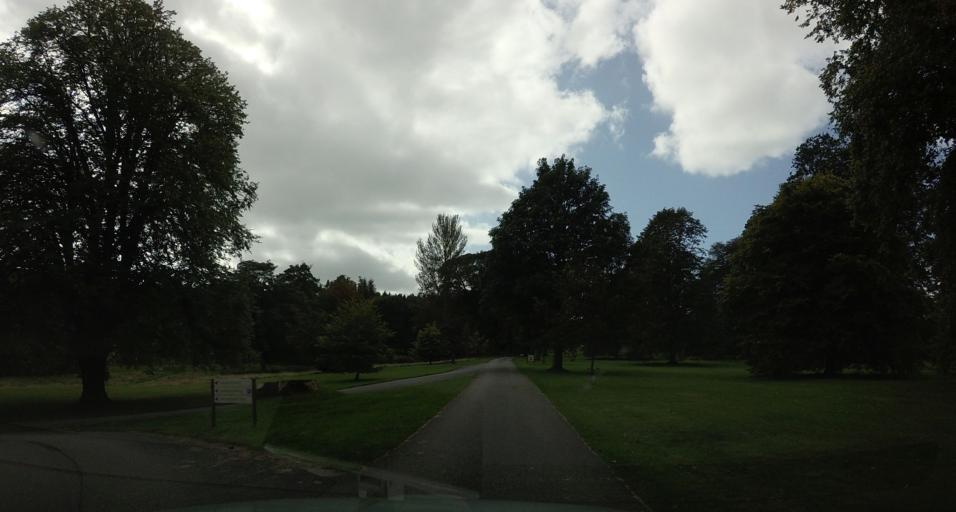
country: GB
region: Scotland
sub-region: Aberdeenshire
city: Kemnay
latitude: 57.2033
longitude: -2.4613
